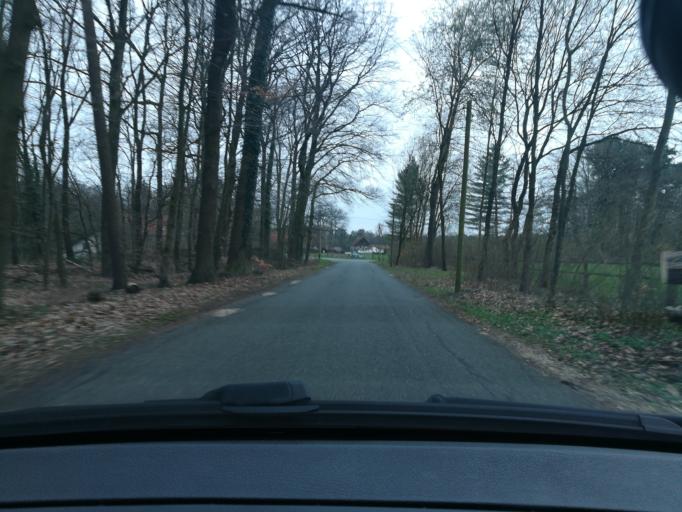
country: DE
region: North Rhine-Westphalia
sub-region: Regierungsbezirk Detmold
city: Oerlinghausen
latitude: 51.9444
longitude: 8.6282
